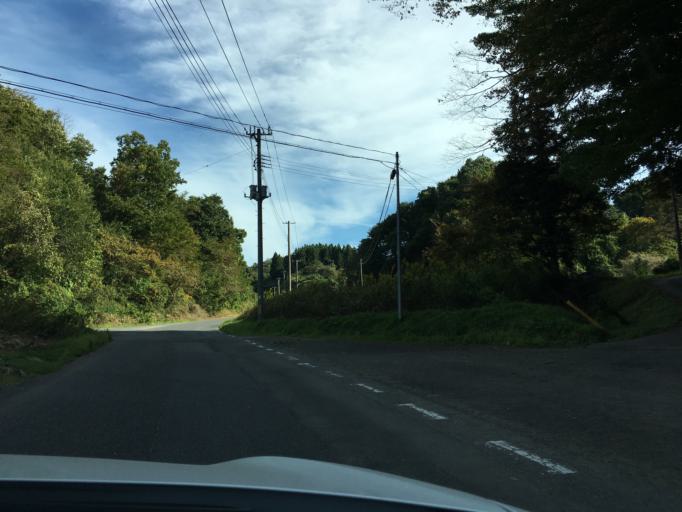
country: JP
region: Fukushima
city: Miharu
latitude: 37.3532
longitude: 140.4866
